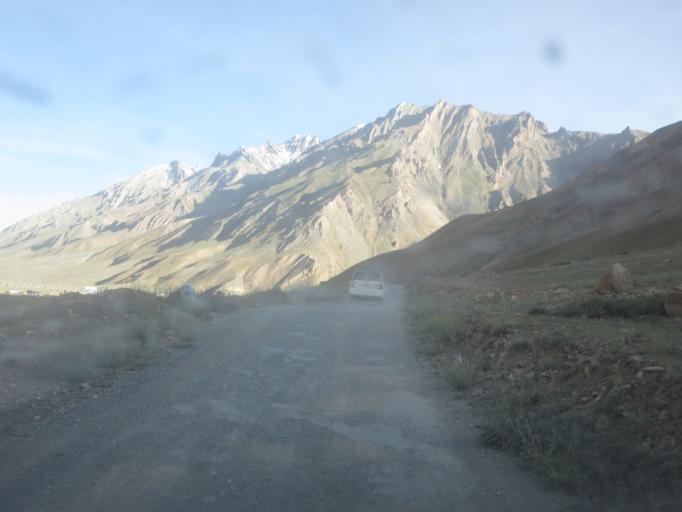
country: IN
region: Himachal Pradesh
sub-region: Kulu
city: Manali
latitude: 32.3400
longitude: 77.9238
